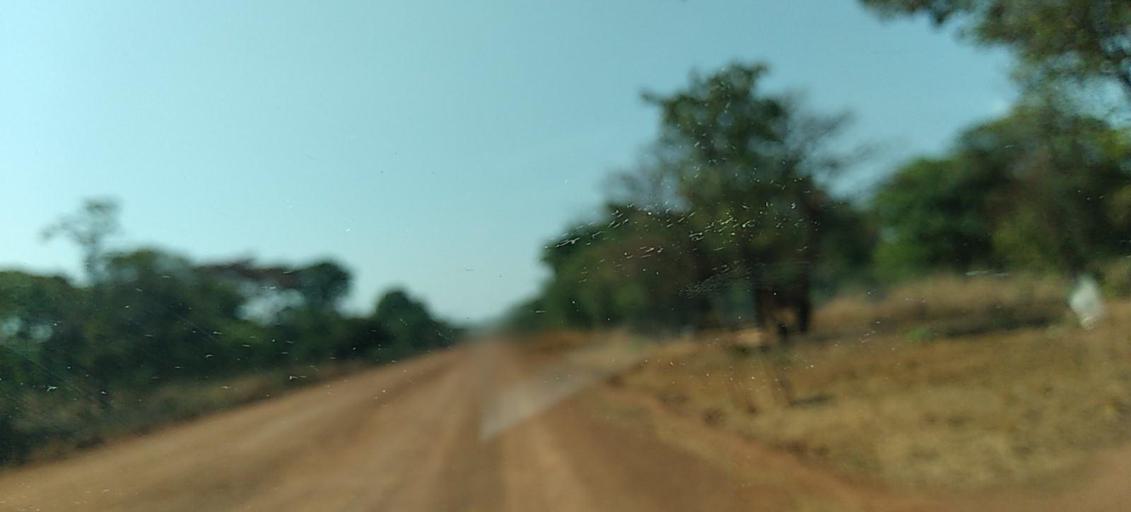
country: ZM
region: North-Western
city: Mwinilunga
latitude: -11.9268
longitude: 25.3213
